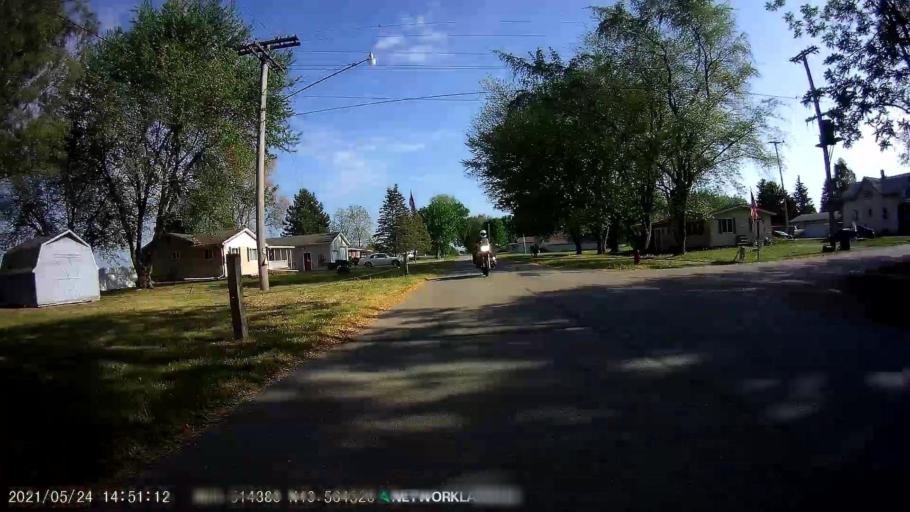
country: US
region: Michigan
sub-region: Tuscola County
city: Caro
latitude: 43.5645
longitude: -83.5144
